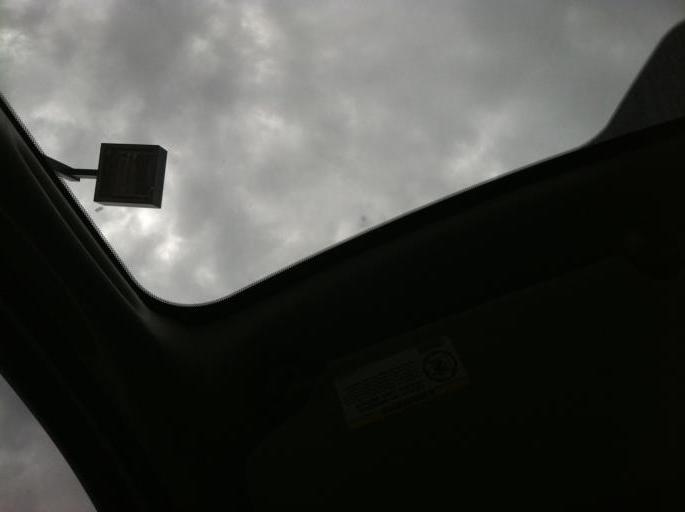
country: US
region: Arizona
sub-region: Gila County
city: Sun Valley
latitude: 34.2542
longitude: -111.2629
